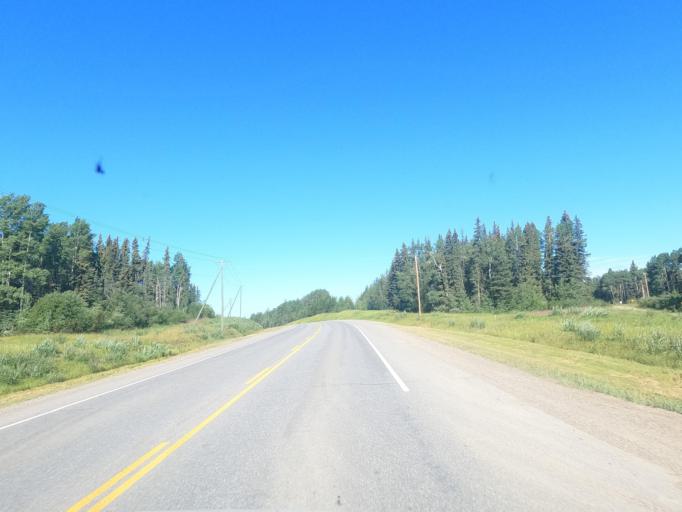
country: CA
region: British Columbia
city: Fort St. John
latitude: 56.6288
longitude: -121.5143
